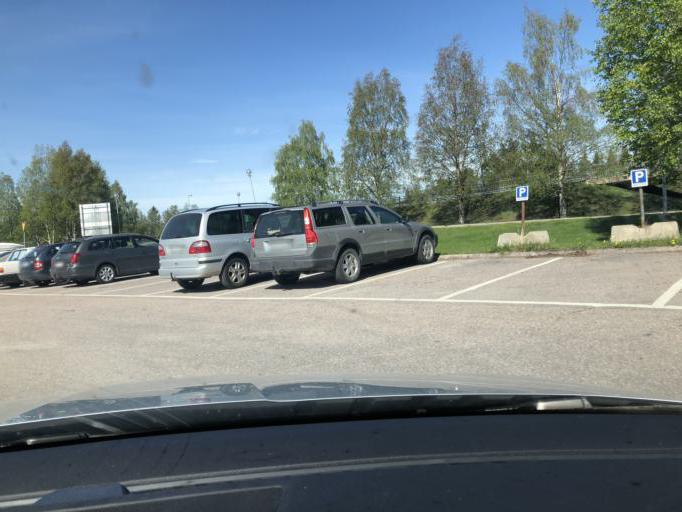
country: SE
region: Norrbotten
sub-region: Gallivare Kommun
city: Gaellivare
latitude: 67.1312
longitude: 20.6848
